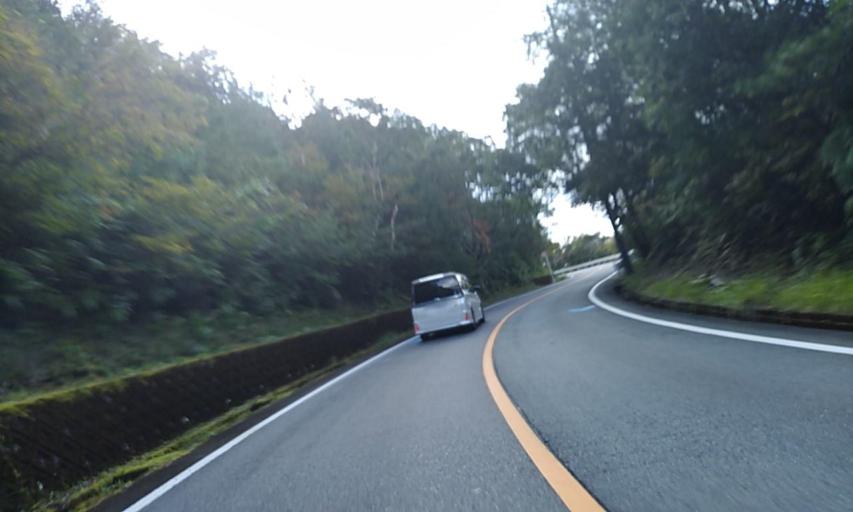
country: JP
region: Mie
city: Owase
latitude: 34.2103
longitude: 136.3539
